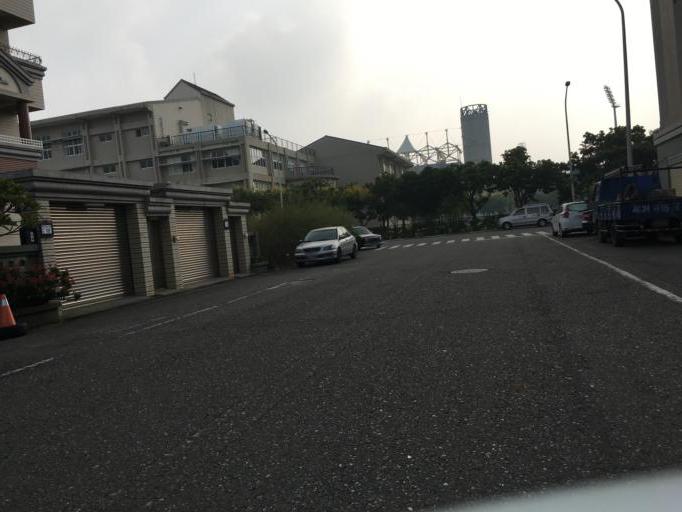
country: TW
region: Taiwan
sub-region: Chiayi
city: Taibao
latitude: 23.4565
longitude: 120.2864
